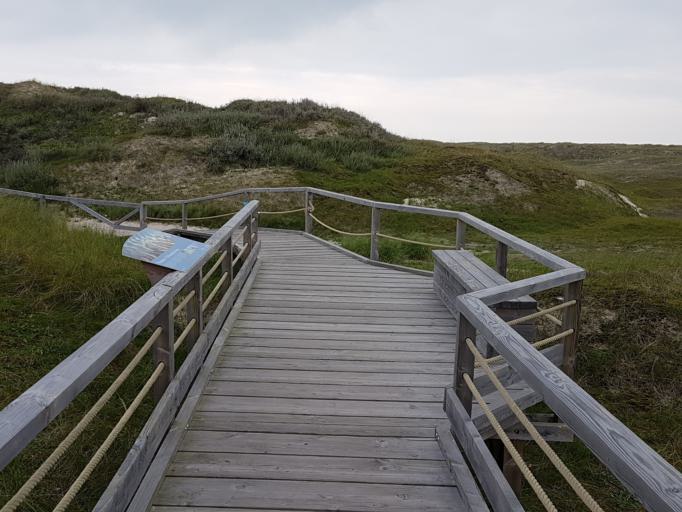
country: DE
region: Lower Saxony
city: Norderney
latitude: 53.7193
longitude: 7.1945
